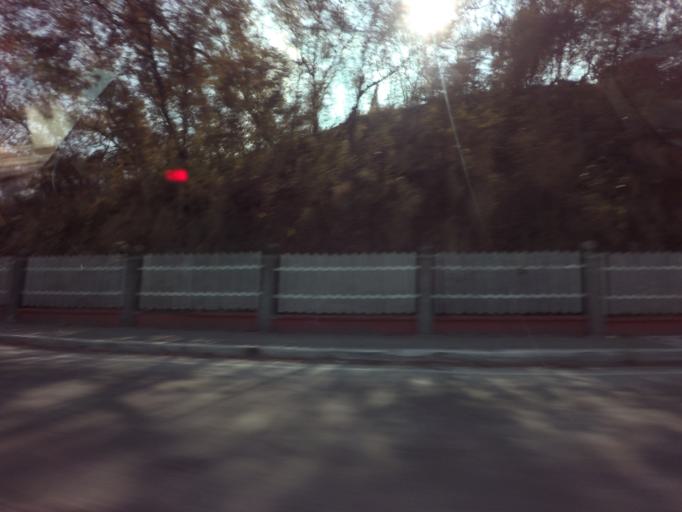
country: PH
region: Metro Manila
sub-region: Makati City
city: Makati City
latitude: 14.5236
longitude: 121.0464
